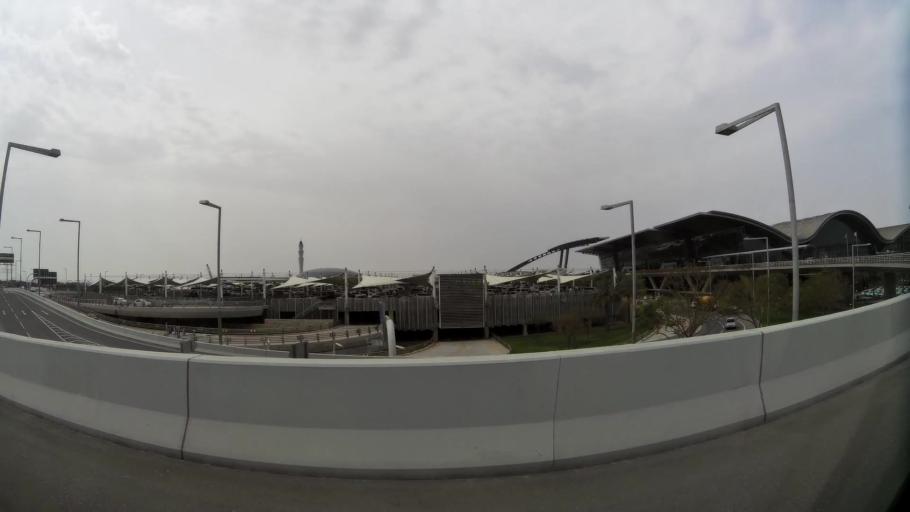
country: QA
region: Al Wakrah
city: Al Wakrah
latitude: 25.2598
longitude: 51.6171
